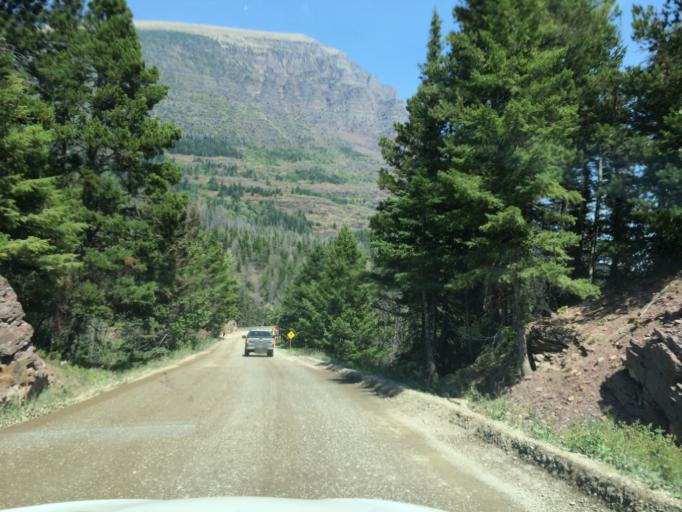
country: US
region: Montana
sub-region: Glacier County
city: Browning
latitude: 48.6765
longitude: -113.5974
